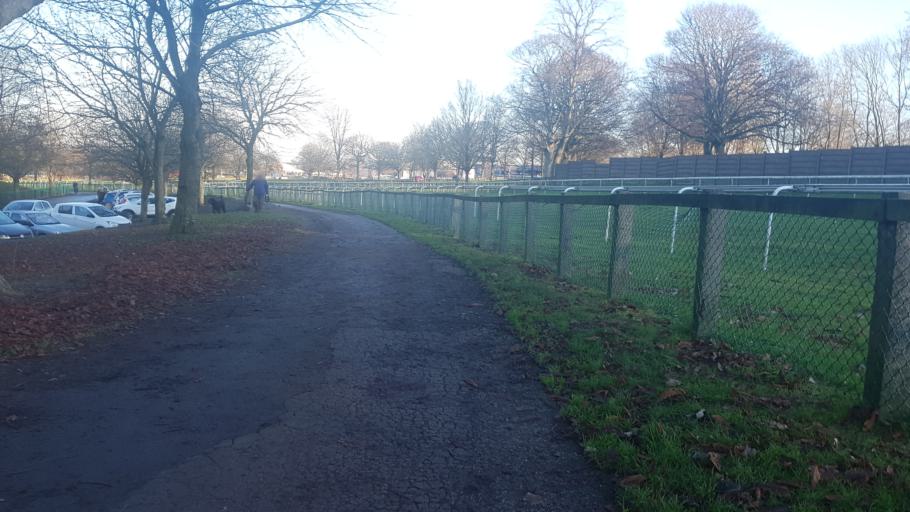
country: GB
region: England
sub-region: City and Borough of Wakefield
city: Pontefract
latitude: 53.6962
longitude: -1.3279
